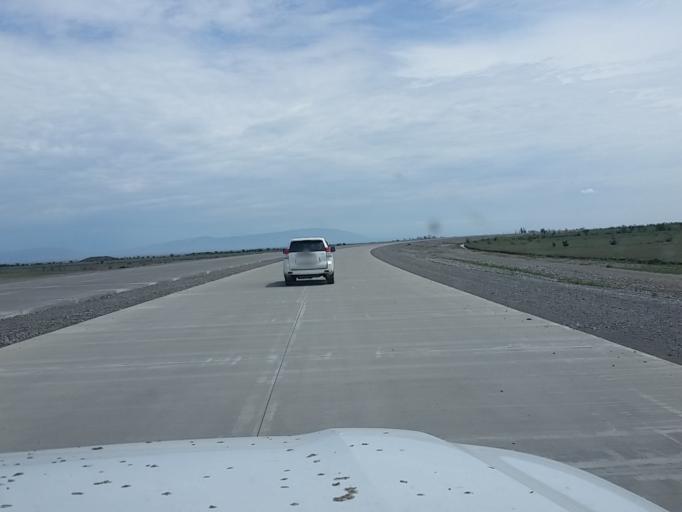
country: KZ
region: Almaty Oblysy
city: Turgen'
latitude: 43.6339
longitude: 78.3786
